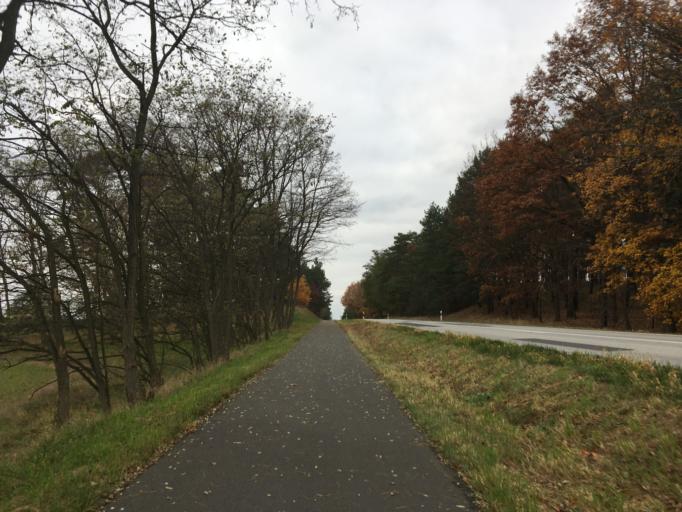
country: DE
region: Brandenburg
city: Mixdorf
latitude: 52.1942
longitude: 14.4620
